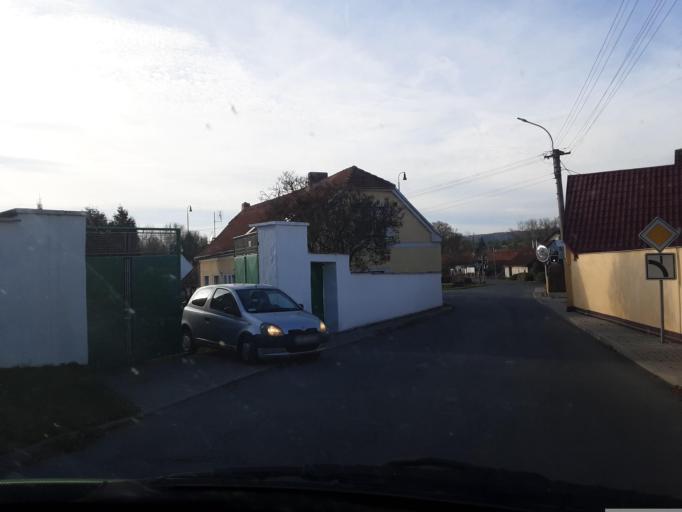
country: CZ
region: Plzensky
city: Horazd'ovice
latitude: 49.2976
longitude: 13.6672
